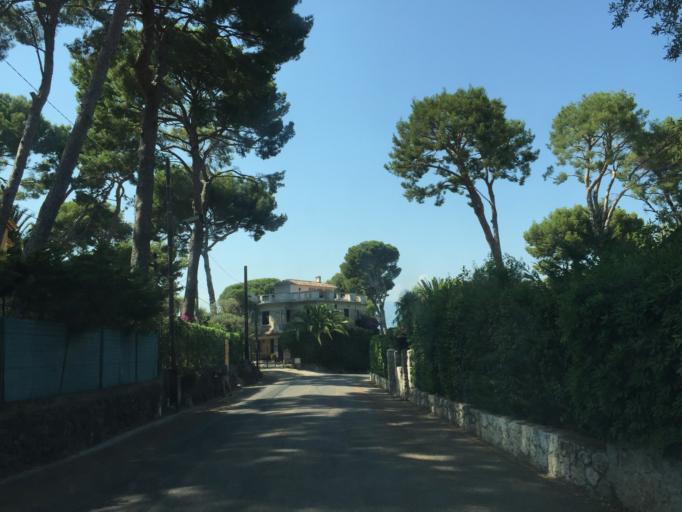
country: FR
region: Provence-Alpes-Cote d'Azur
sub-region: Departement des Alpes-Maritimes
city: Antibes
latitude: 43.5677
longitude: 7.1338
